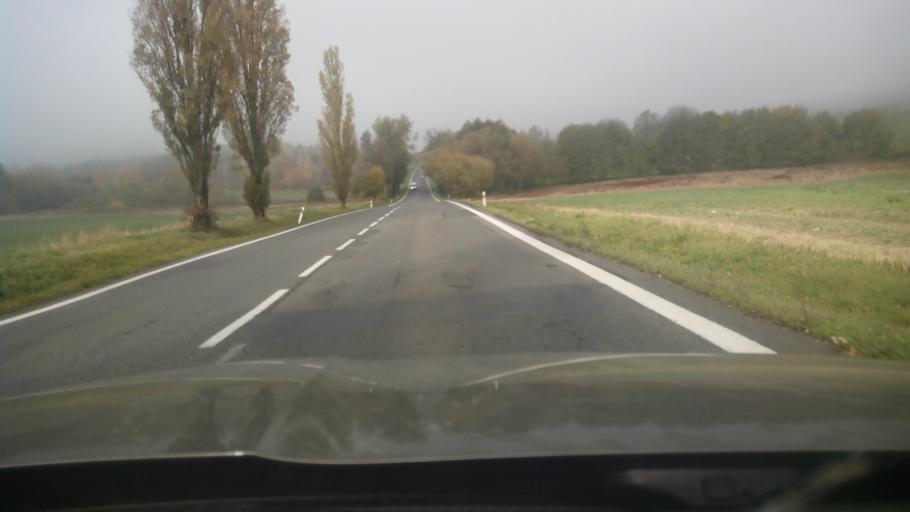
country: CZ
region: Central Bohemia
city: Milin
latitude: 49.6150
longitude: 14.0560
